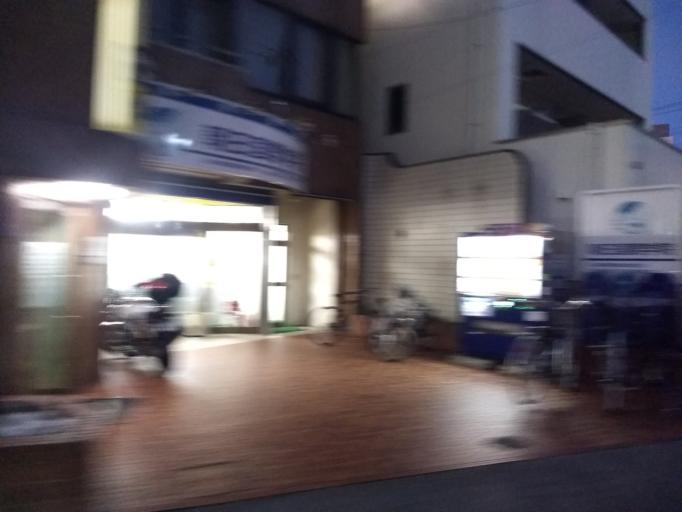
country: JP
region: Chiba
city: Kashiwa
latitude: 35.8647
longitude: 139.9666
